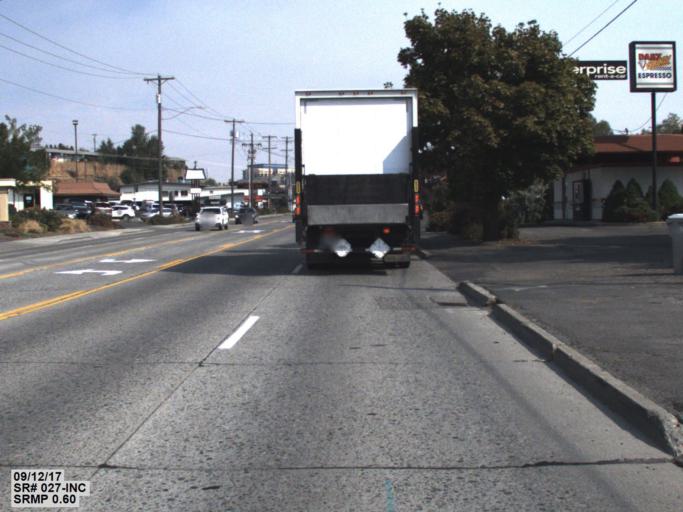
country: US
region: Washington
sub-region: Whitman County
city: Pullman
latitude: 46.7377
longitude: -117.1742
